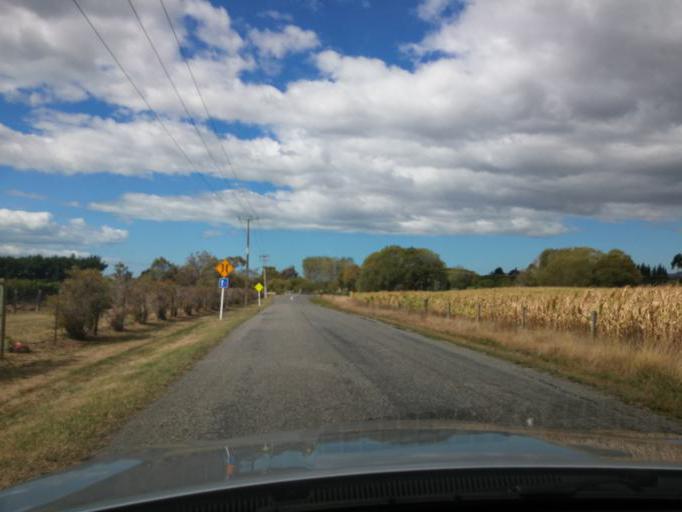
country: NZ
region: Marlborough
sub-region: Marlborough District
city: Blenheim
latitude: -41.5265
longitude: 173.8343
